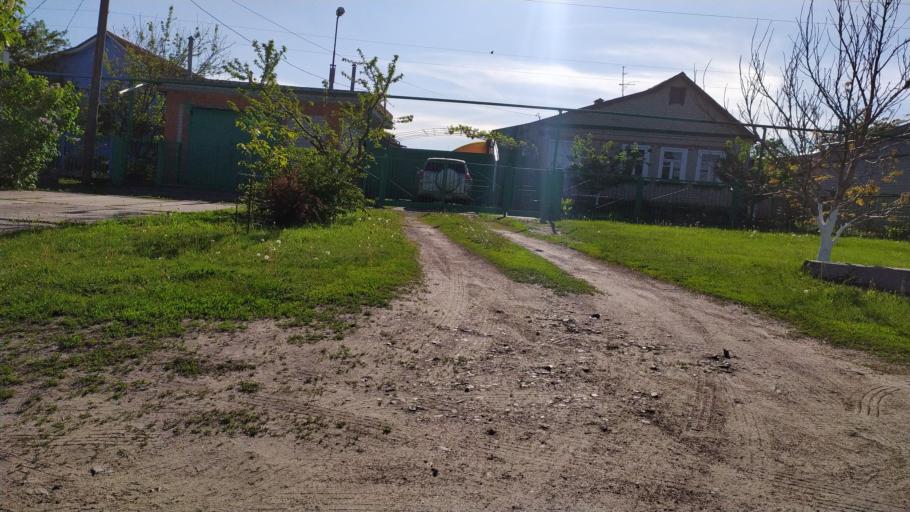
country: RU
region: Kursk
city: Kursk
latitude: 51.6372
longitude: 36.1491
